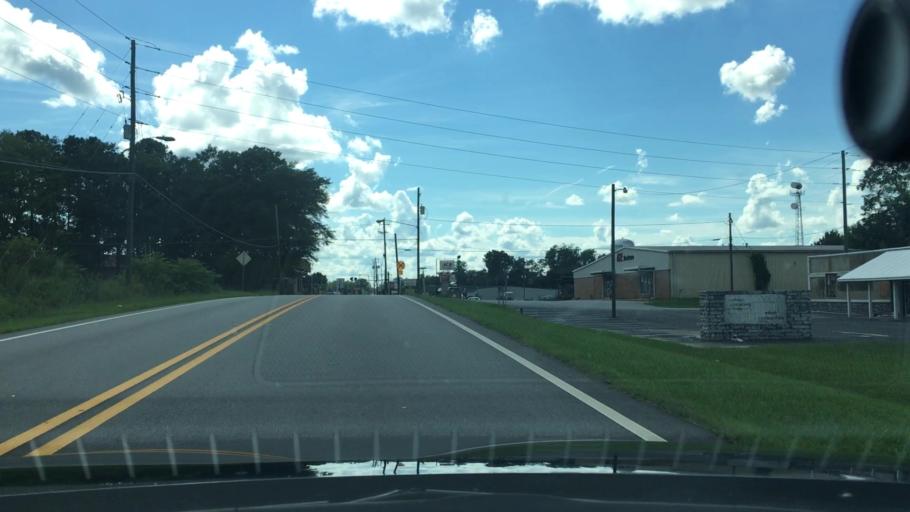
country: US
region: Georgia
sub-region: Butts County
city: Jackson
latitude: 33.2945
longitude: -83.9516
